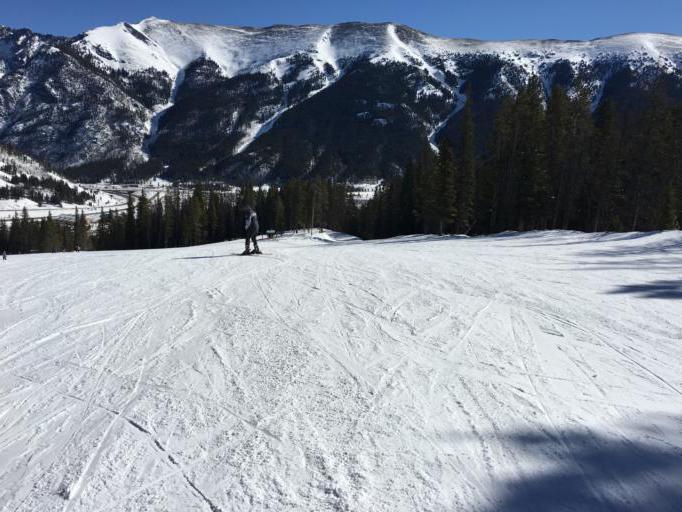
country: US
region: Colorado
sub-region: Summit County
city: Frisco
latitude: 39.4943
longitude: -106.1589
